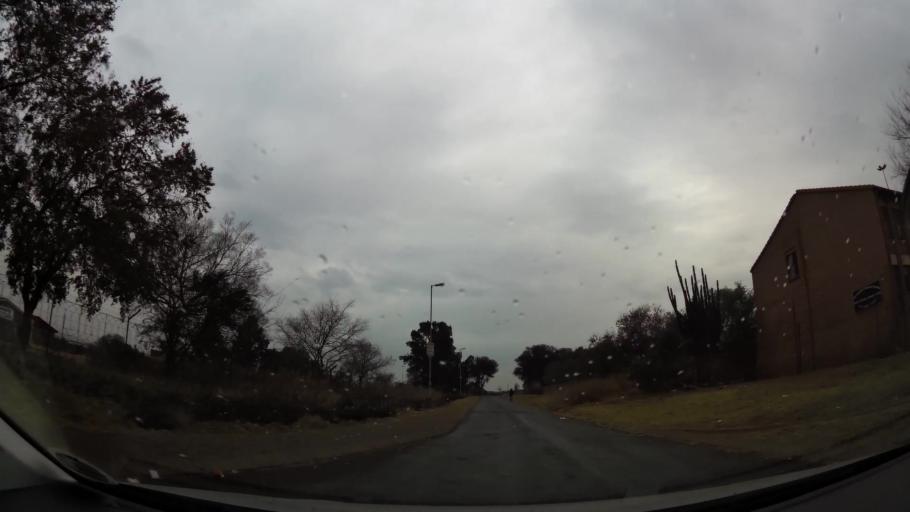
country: ZA
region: Gauteng
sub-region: City of Johannesburg Metropolitan Municipality
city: Soweto
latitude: -26.2442
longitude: 27.8763
